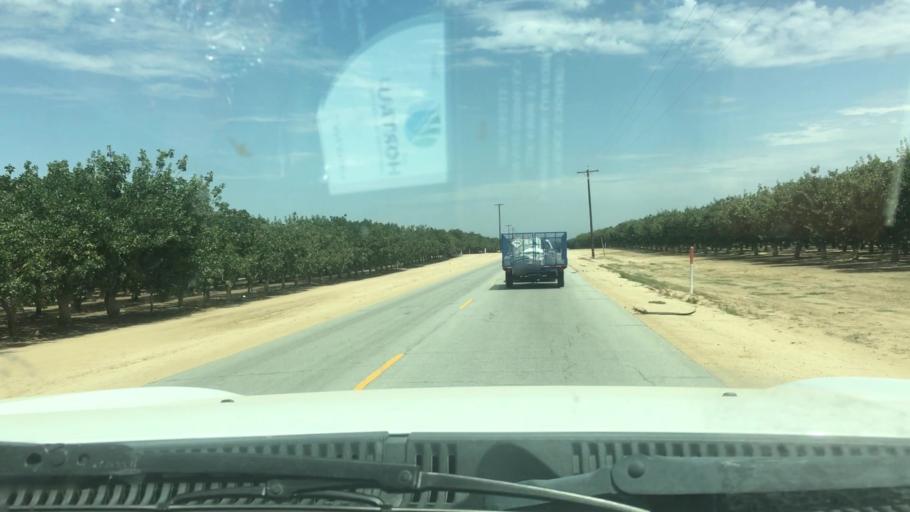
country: US
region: California
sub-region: Kern County
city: McFarland
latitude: 35.5967
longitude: -119.1510
